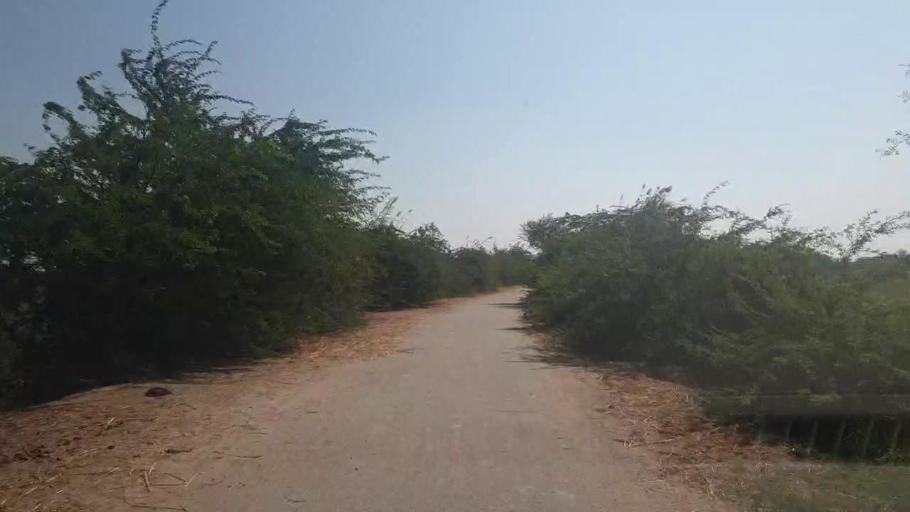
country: PK
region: Sindh
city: Badin
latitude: 24.6414
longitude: 68.9122
